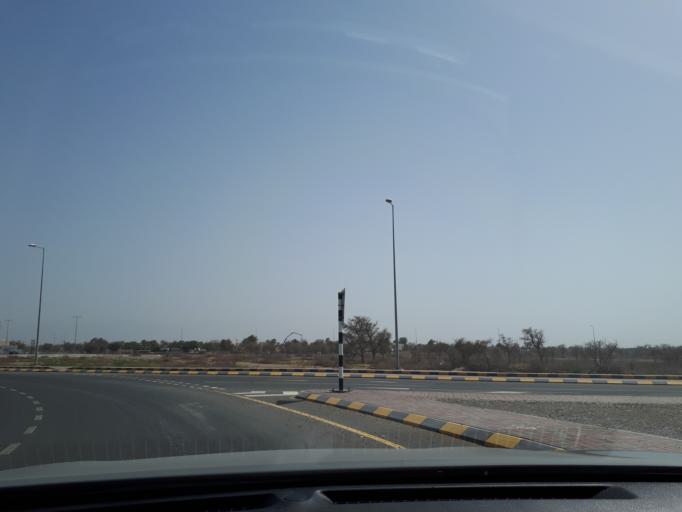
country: OM
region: Al Batinah
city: Barka'
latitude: 23.6976
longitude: 57.9618
